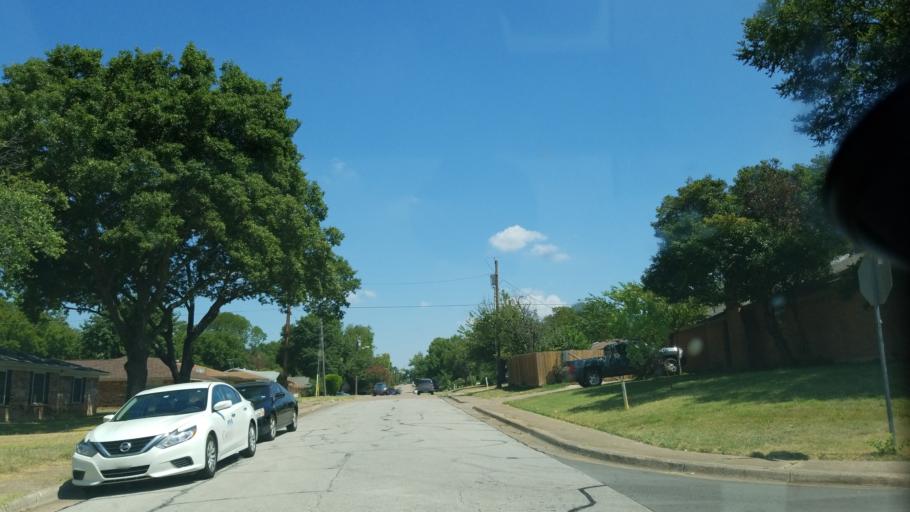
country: US
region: Texas
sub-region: Dallas County
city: Duncanville
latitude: 32.6542
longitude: -96.8993
